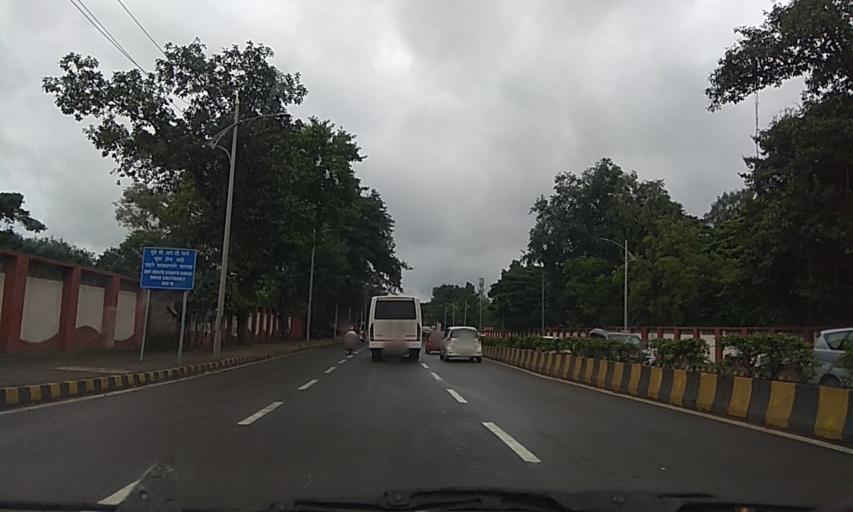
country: IN
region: Maharashtra
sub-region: Pune Division
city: Khadki
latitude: 18.5507
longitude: 73.8683
